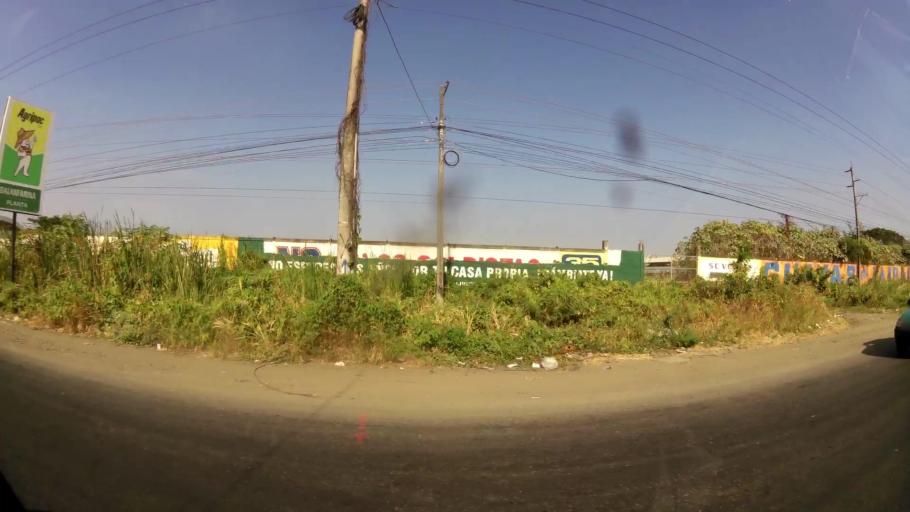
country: EC
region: Guayas
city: Eloy Alfaro
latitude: -2.1875
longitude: -79.8279
